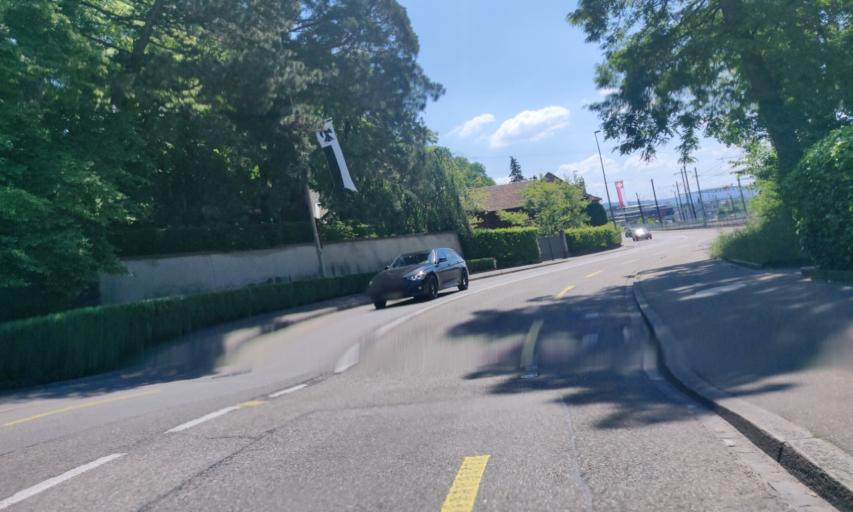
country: CH
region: Basel-Landschaft
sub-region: Bezirk Arlesheim
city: Munchenstein
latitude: 47.5181
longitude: 7.6190
